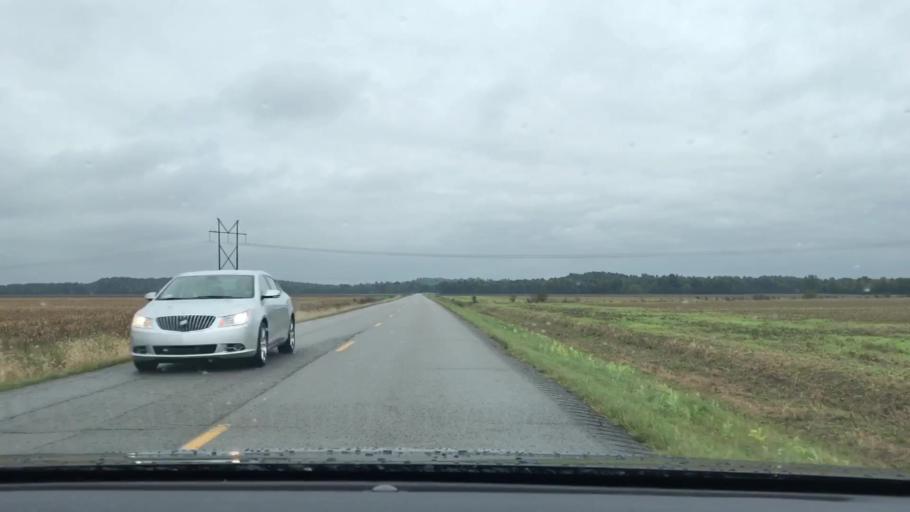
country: US
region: Kentucky
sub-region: McLean County
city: Calhoun
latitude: 37.5055
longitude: -87.2503
